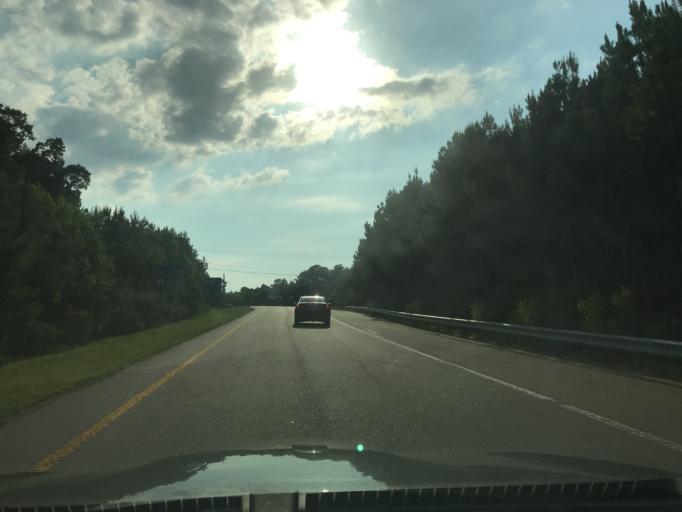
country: US
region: North Carolina
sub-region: Wake County
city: Cary
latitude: 35.9122
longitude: -78.7260
